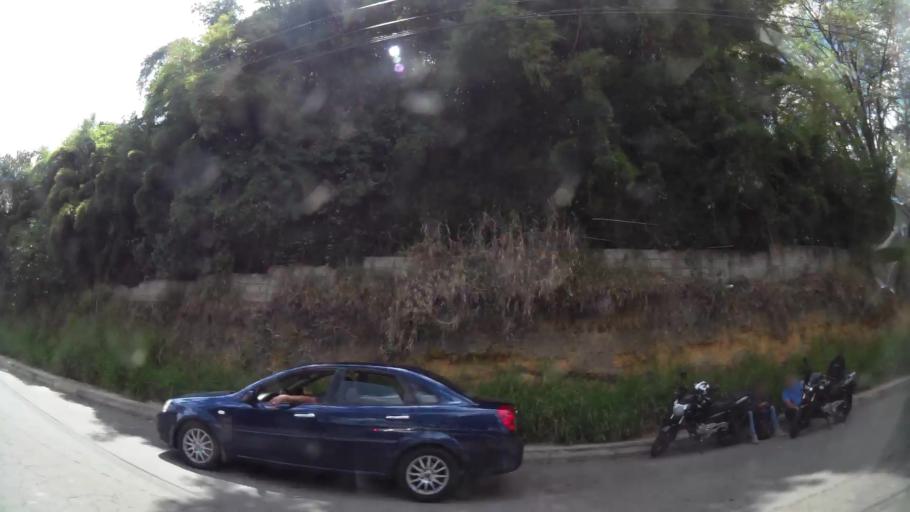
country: CO
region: Antioquia
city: La Estrella
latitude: 6.1589
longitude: -75.6322
